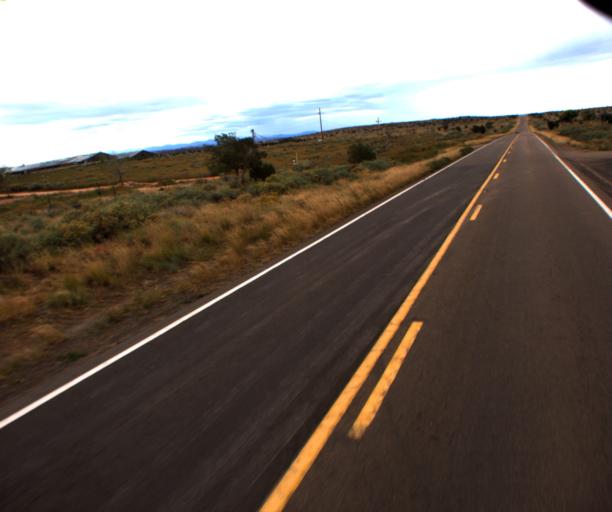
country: US
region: Arizona
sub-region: Navajo County
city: Snowflake
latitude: 34.5623
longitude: -110.0817
